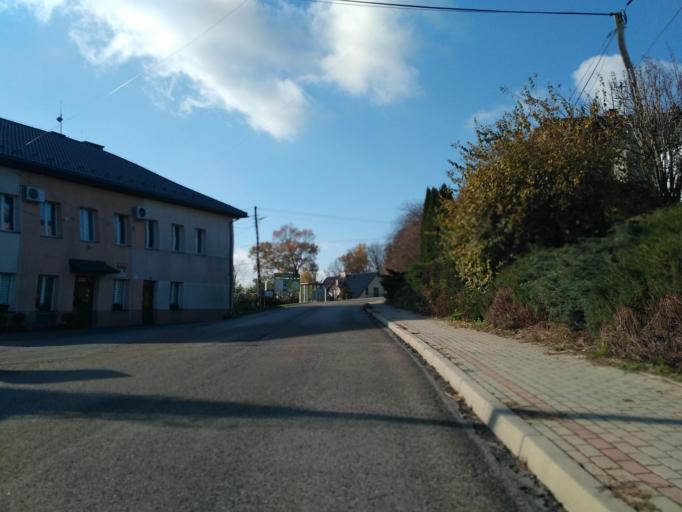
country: PL
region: Subcarpathian Voivodeship
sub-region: Powiat rzeszowski
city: Zglobien
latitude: 50.0249
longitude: 21.8747
